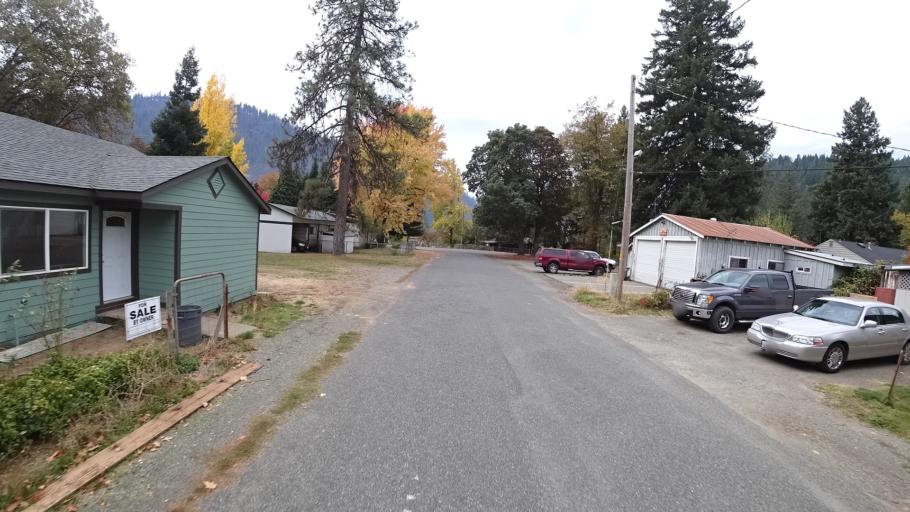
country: US
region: California
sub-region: Siskiyou County
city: Happy Camp
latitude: 41.7978
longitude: -123.3766
